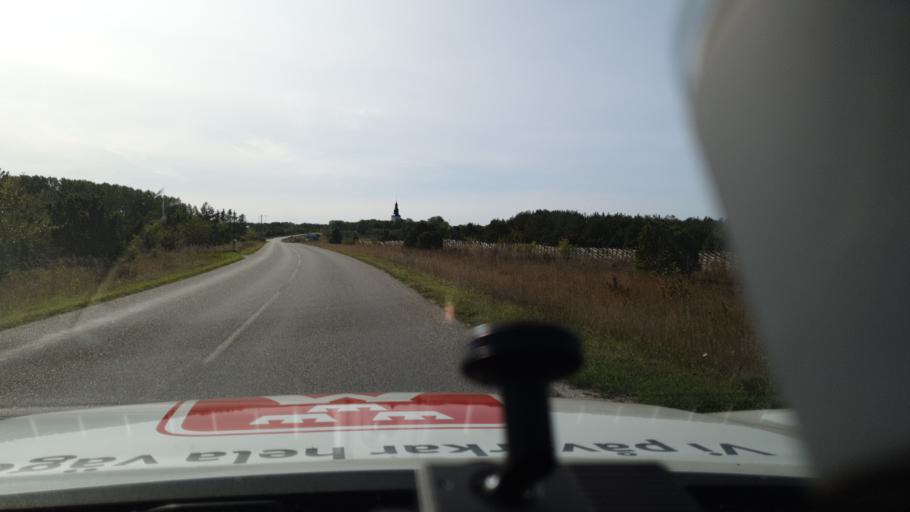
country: SE
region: Gotland
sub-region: Gotland
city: Slite
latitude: 57.9209
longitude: 19.1392
